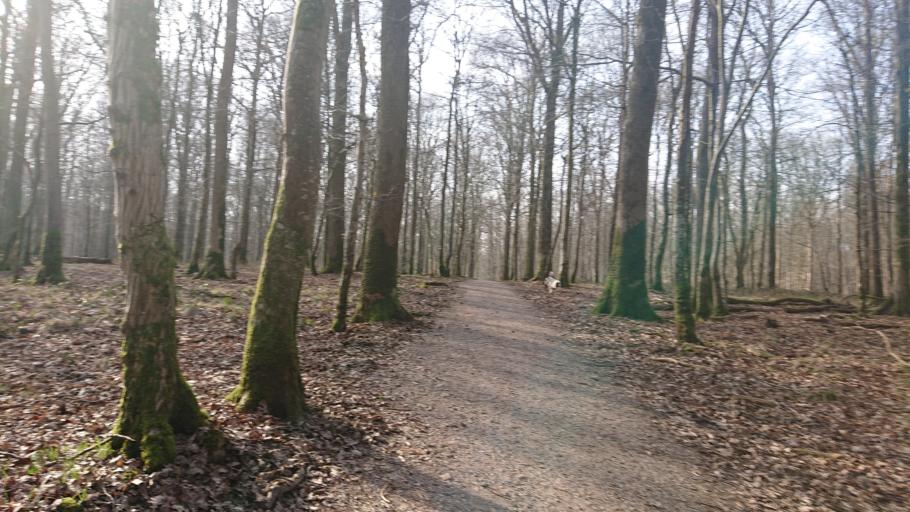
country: FR
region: Nord-Pas-de-Calais
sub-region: Departement du Nord
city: Maroilles
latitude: 50.1713
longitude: 3.7222
